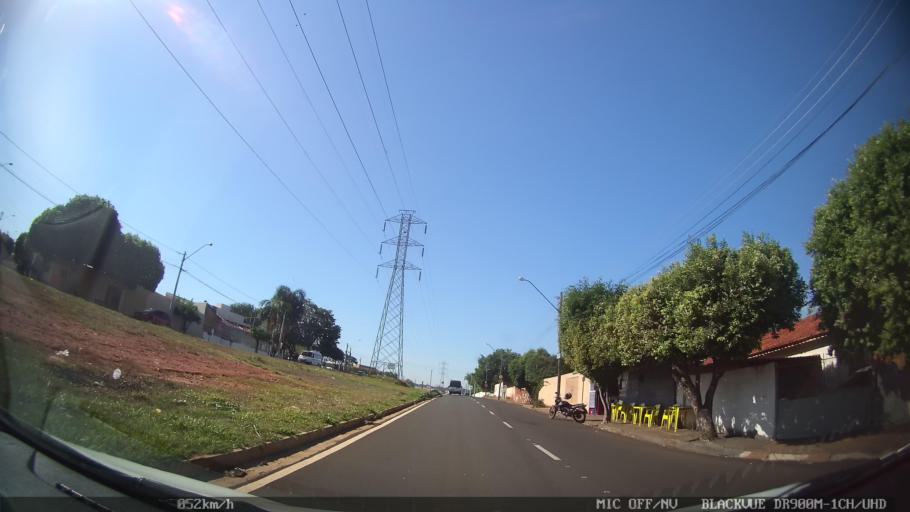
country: BR
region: Sao Paulo
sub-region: Sao Jose Do Rio Preto
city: Sao Jose do Rio Preto
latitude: -20.7635
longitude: -49.3638
